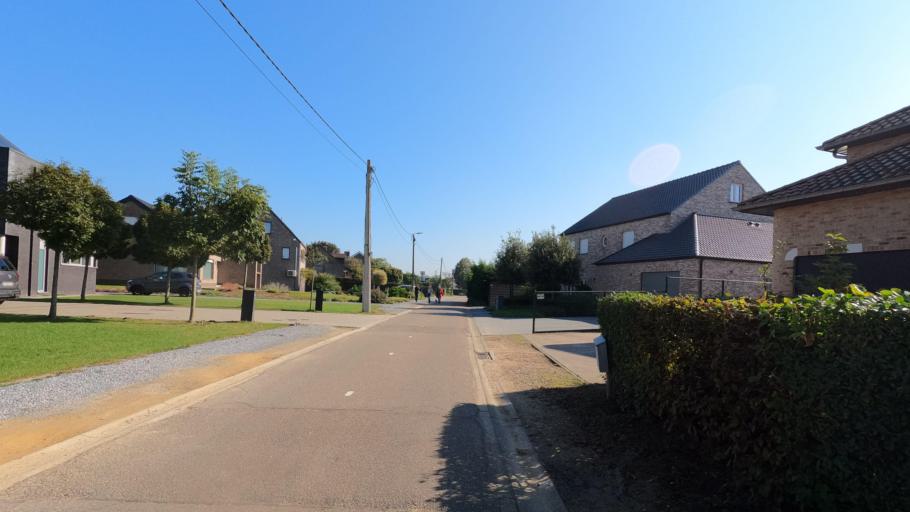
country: BE
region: Flanders
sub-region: Provincie Vlaams-Brabant
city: Rotselaar
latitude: 50.9468
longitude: 4.7411
